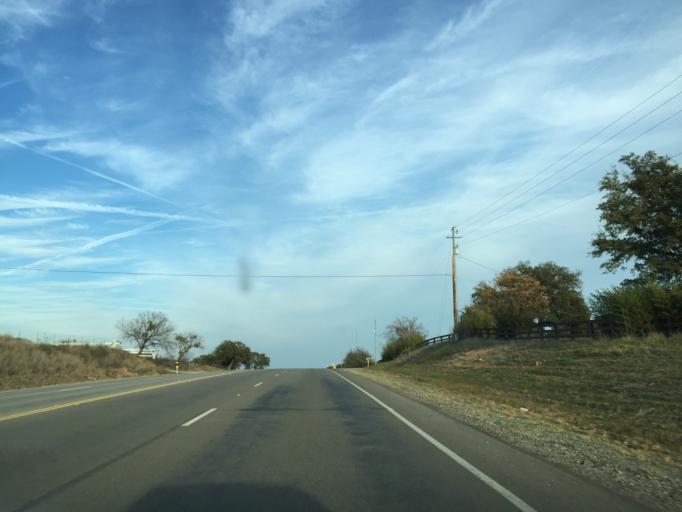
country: US
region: Texas
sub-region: Llano County
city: Llano
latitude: 30.7599
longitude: -98.6596
